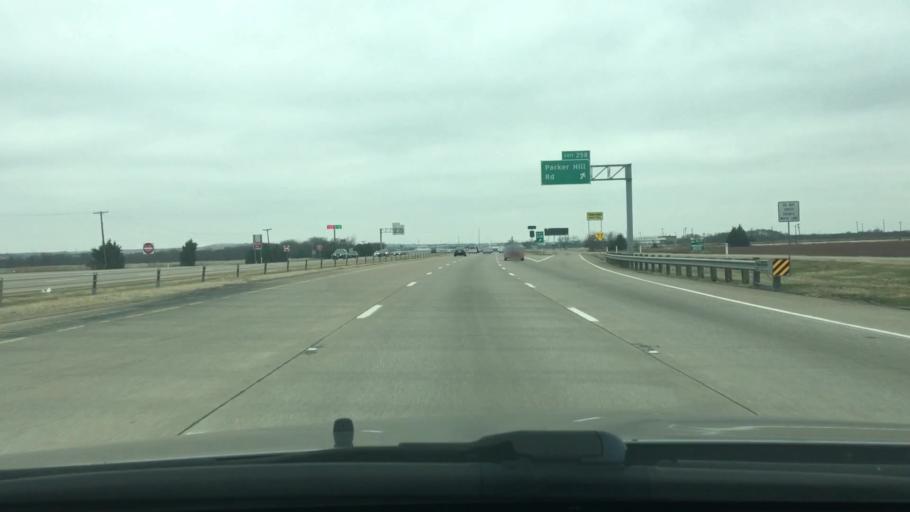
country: US
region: Texas
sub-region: Ellis County
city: Palmer
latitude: 32.4230
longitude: -96.6588
